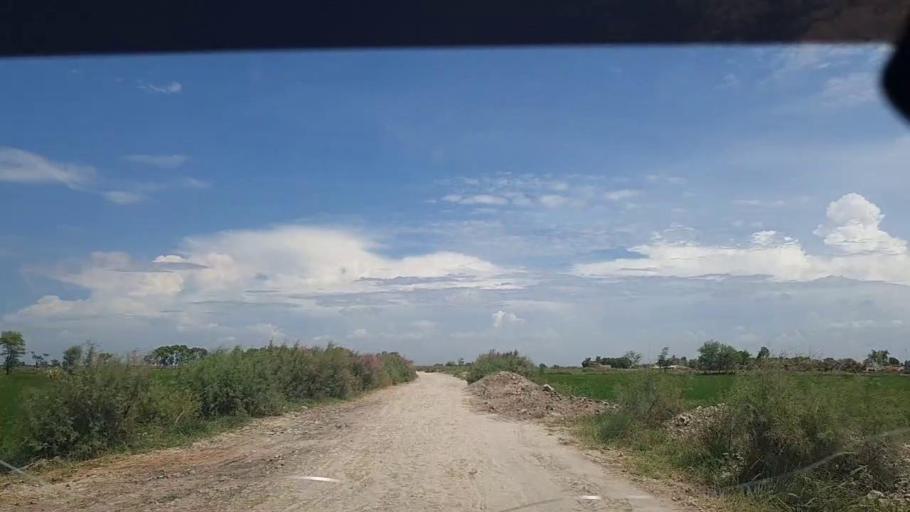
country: PK
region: Sindh
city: Ghauspur
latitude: 28.1499
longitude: 68.9637
